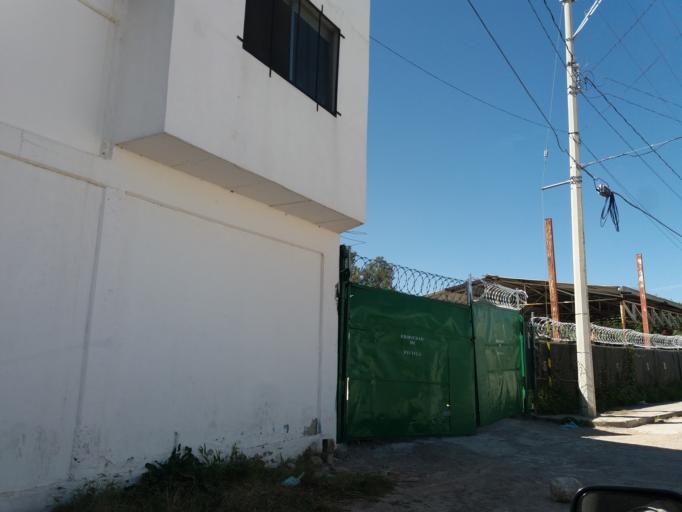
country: MX
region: Aguascalientes
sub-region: Aguascalientes
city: San Sebastian [Fraccionamiento]
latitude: 21.8001
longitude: -102.2758
